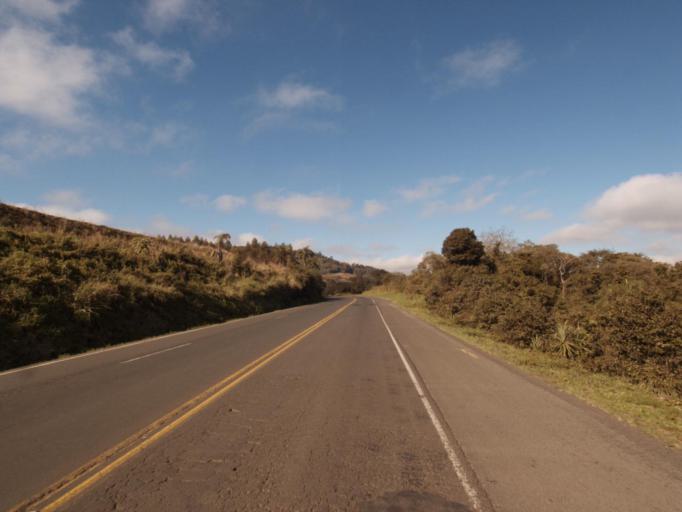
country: BR
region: Rio Grande do Sul
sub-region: Frederico Westphalen
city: Frederico Westphalen
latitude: -27.0743
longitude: -53.2315
